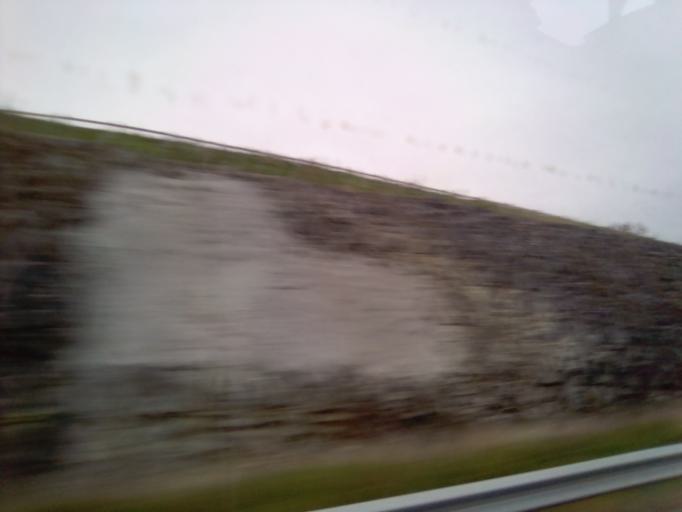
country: IE
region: Connaught
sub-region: County Galway
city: Oranmore
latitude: 53.2034
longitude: -8.8273
